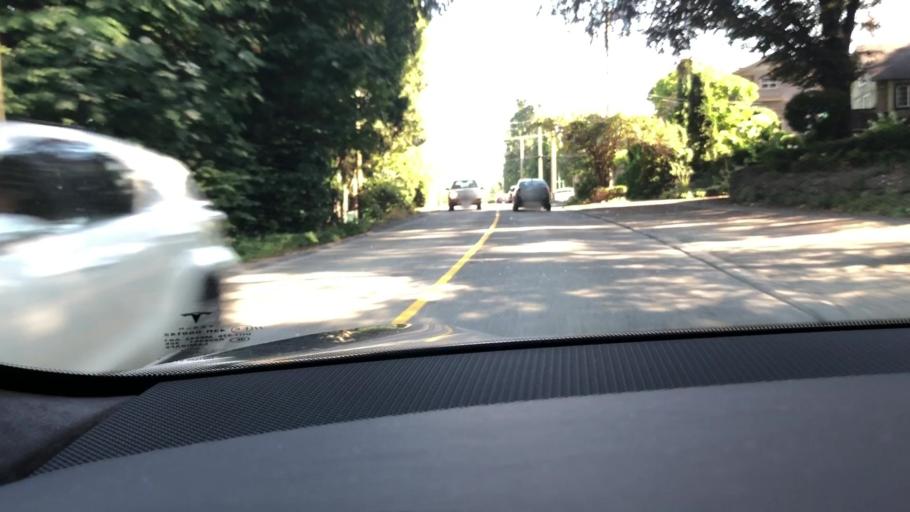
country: CA
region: British Columbia
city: Burnaby
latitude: 49.2526
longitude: -122.9819
